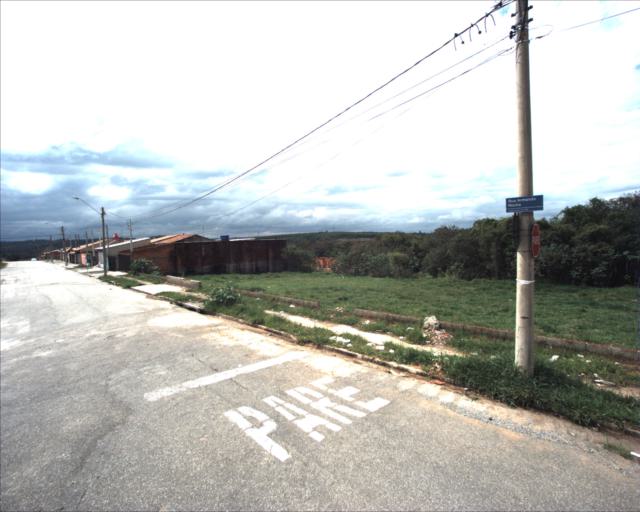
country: BR
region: Sao Paulo
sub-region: Sorocaba
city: Sorocaba
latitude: -23.4233
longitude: -47.4628
